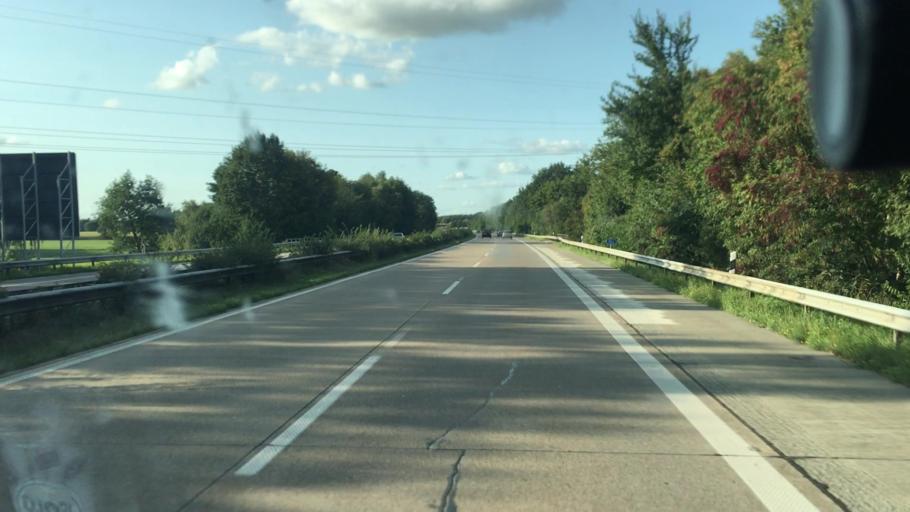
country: DE
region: Lower Saxony
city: Rastede
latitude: 53.2520
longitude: 8.1737
